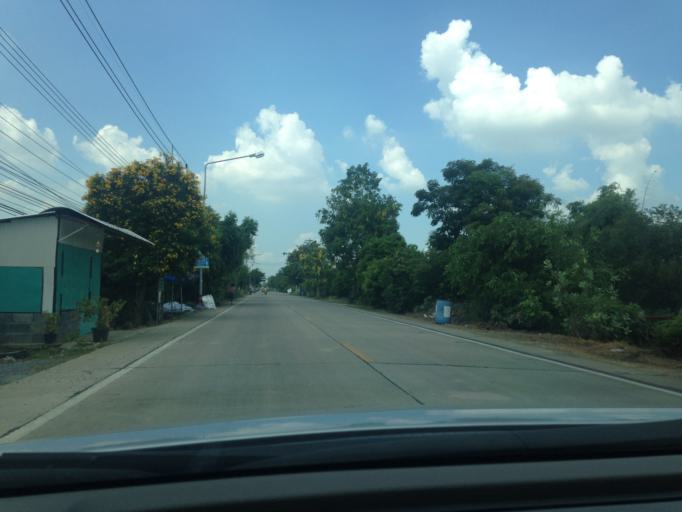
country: TH
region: Pathum Thani
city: Khlong Luang
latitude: 14.0428
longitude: 100.5917
